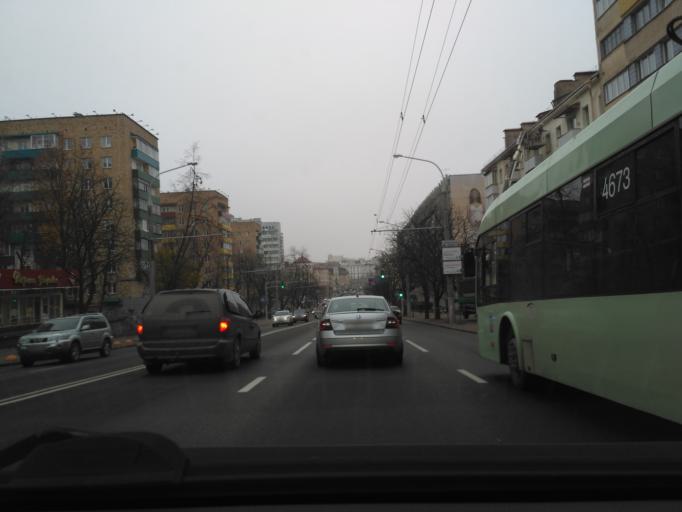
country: BY
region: Minsk
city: Minsk
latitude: 53.9037
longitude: 27.5442
